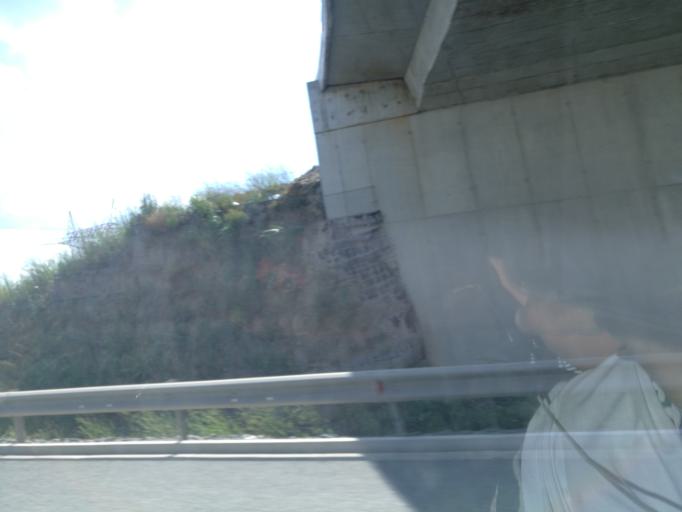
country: RO
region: Constanta
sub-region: Municipiul Constanta
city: Palazu Mare
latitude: 44.2165
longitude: 28.5520
